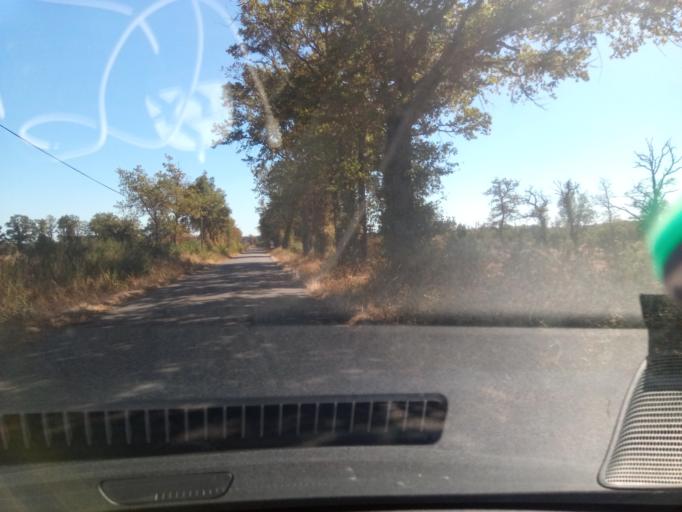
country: FR
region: Poitou-Charentes
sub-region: Departement de la Vienne
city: Saulge
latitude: 46.3789
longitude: 0.8986
